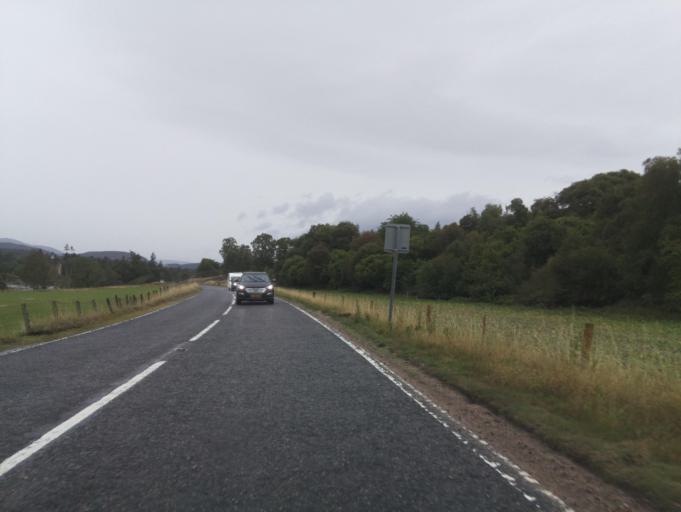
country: GB
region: Scotland
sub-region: Aberdeenshire
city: Ballater
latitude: 57.0469
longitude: -3.1694
